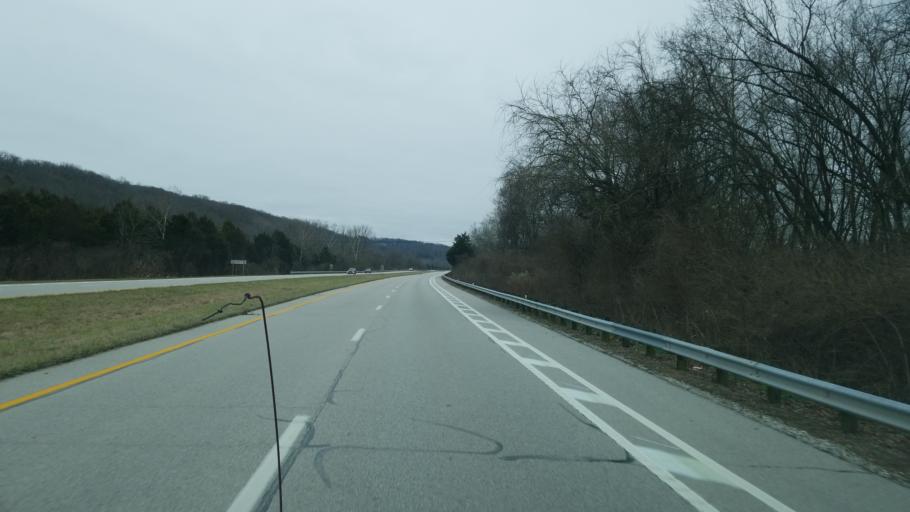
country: US
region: Ohio
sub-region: Hamilton County
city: Cherry Grove
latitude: 39.0331
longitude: -84.3319
